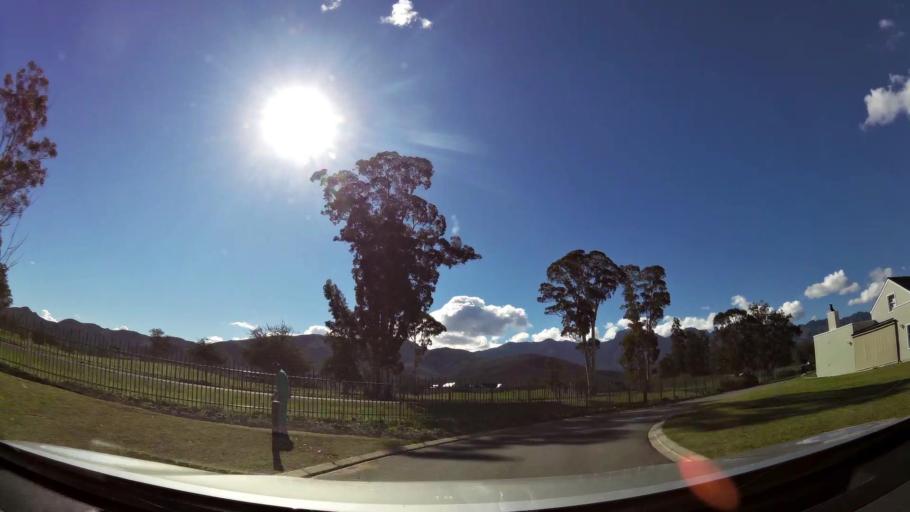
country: ZA
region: Western Cape
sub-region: Cape Winelands District Municipality
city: Ashton
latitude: -33.8110
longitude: 19.8545
